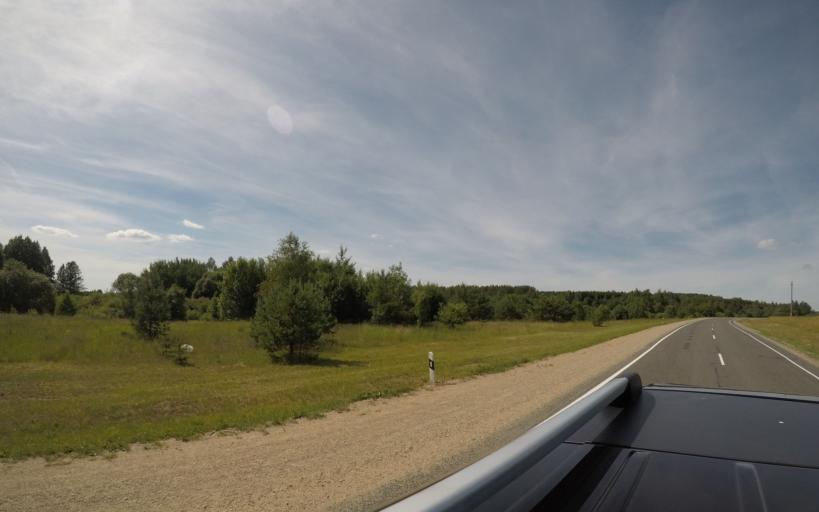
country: BY
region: Grodnenskaya
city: Hal'shany
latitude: 54.2629
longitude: 25.9878
